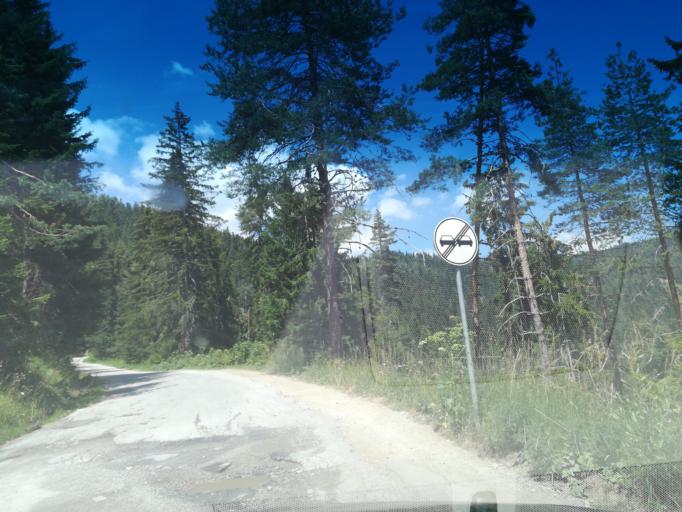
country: BG
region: Smolyan
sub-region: Obshtina Chepelare
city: Chepelare
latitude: 41.6814
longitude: 24.7708
